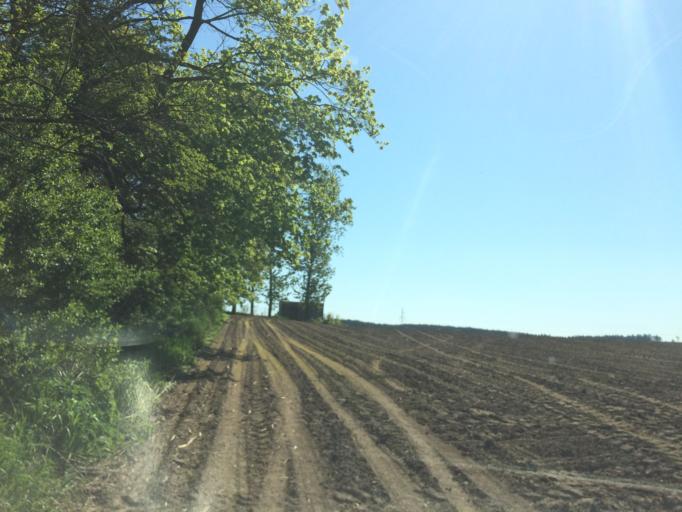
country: PL
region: Warmian-Masurian Voivodeship
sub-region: Powiat nowomiejski
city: Biskupiec
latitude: 53.5345
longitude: 19.4604
